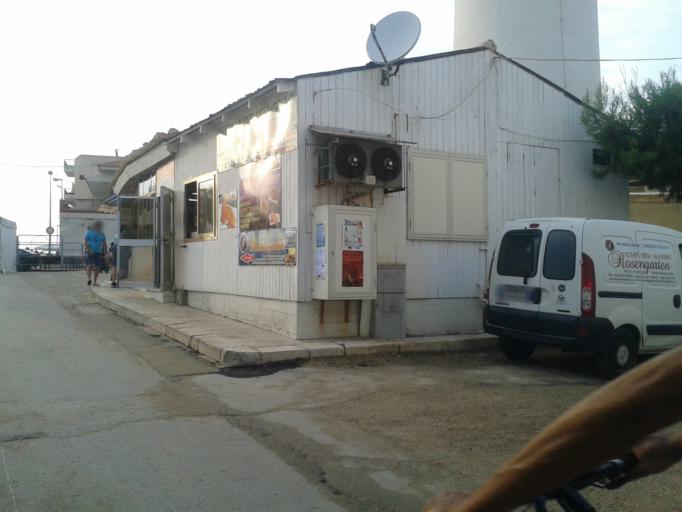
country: IT
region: Sicily
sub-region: Ragusa
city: Santa Croce Camerina
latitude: 36.7871
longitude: 14.4941
